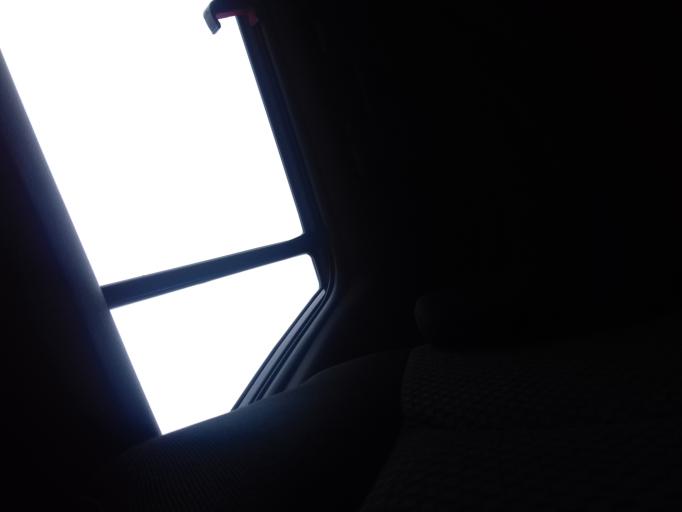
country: IE
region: Leinster
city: Portraine
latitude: 53.4794
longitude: -6.1210
